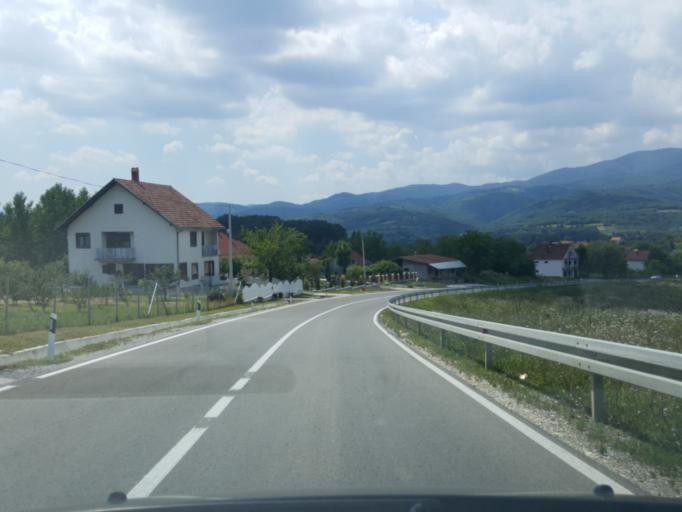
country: RS
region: Central Serbia
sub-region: Sumadijski Okrug
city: Topola
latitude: 44.2027
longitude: 20.6118
